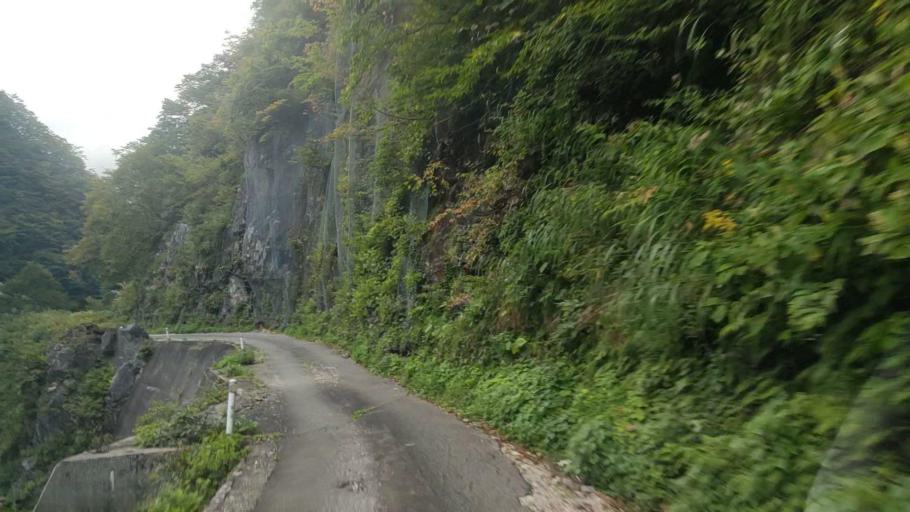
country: JP
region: Toyama
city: Yatsuomachi-higashikumisaka
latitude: 36.3917
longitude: 137.0800
